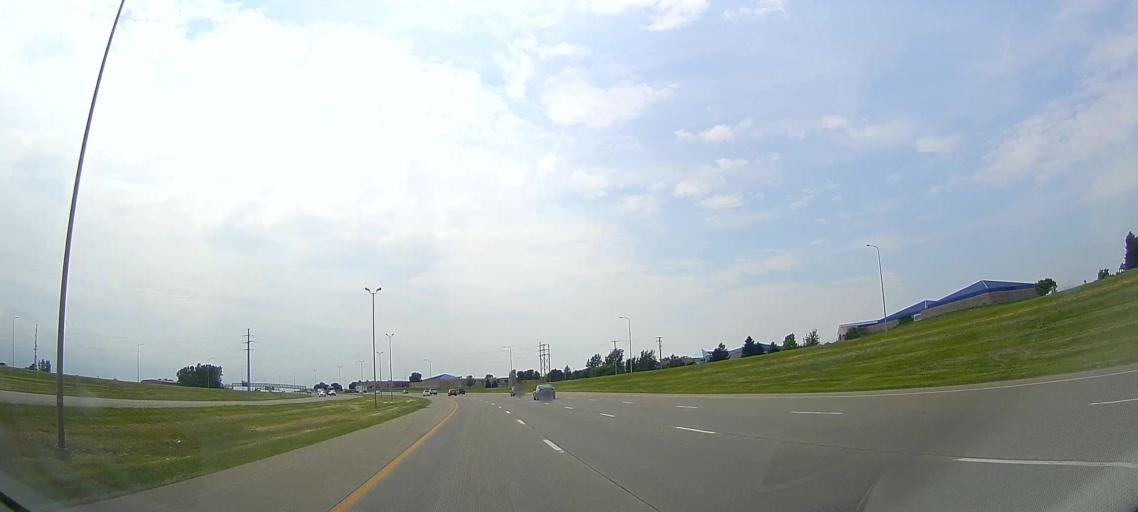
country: US
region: South Dakota
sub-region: Minnehaha County
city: Sioux Falls
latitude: 43.5710
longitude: -96.7765
